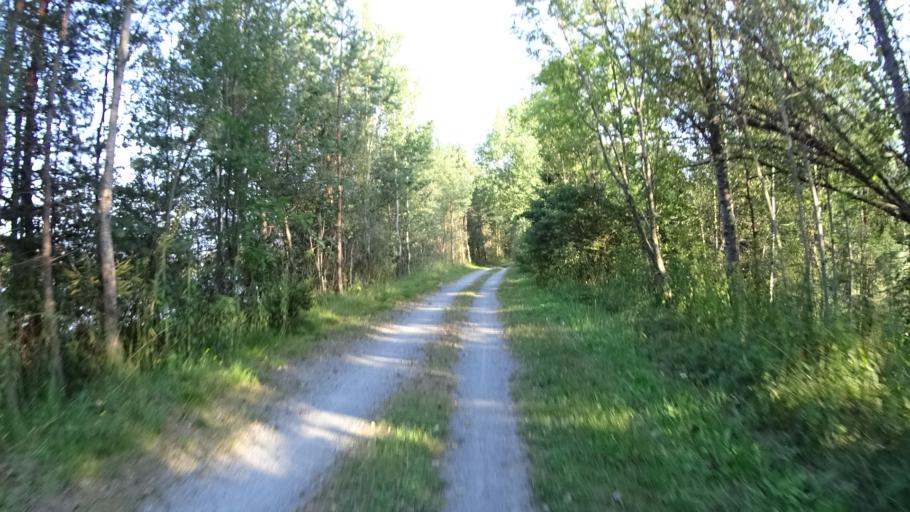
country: AT
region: Carinthia
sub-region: Politischer Bezirk Villach Land
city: Sankt Jakob
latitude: 46.5458
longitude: 14.0880
